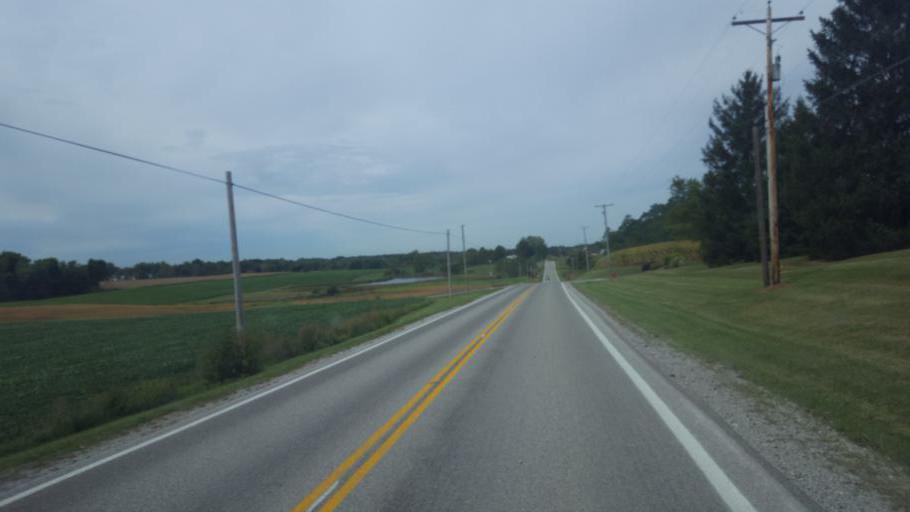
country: US
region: Ohio
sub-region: Knox County
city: Centerburg
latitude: 40.3997
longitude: -82.7306
